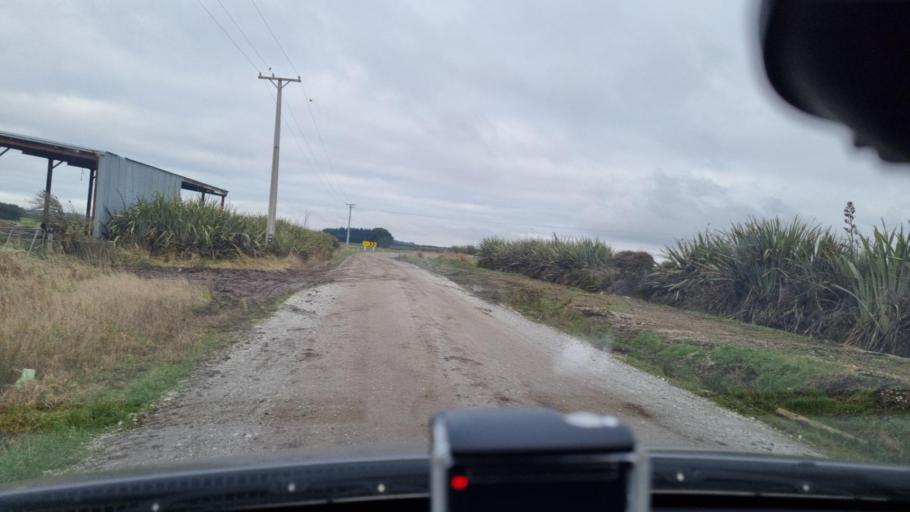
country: NZ
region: Southland
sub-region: Invercargill City
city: Bluff
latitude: -46.5283
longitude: 168.4104
